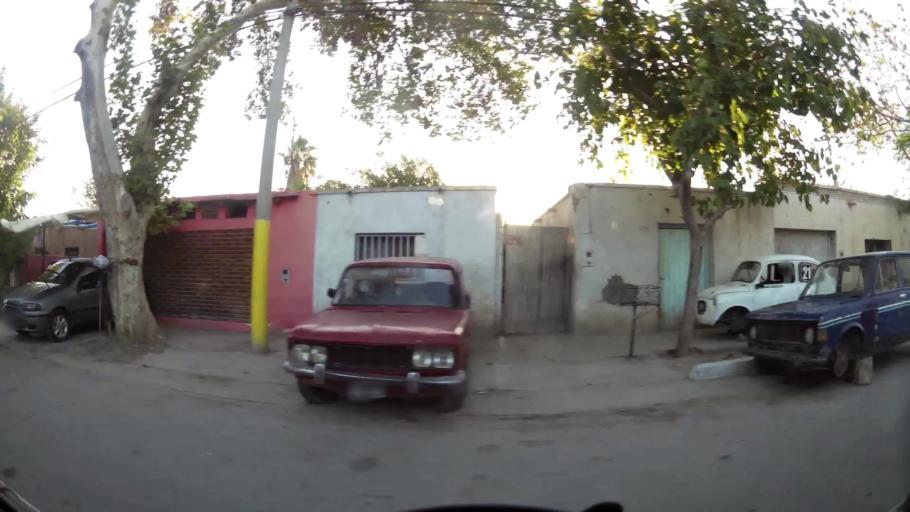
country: AR
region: San Juan
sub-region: Departamento de Santa Lucia
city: Santa Lucia
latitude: -31.5225
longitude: -68.5078
